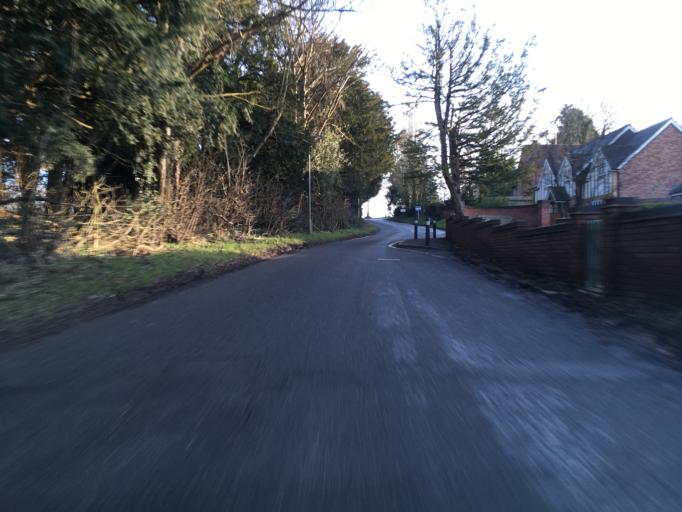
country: GB
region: England
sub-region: Warwickshire
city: Stratford-upon-Avon
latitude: 52.2335
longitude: -1.6853
